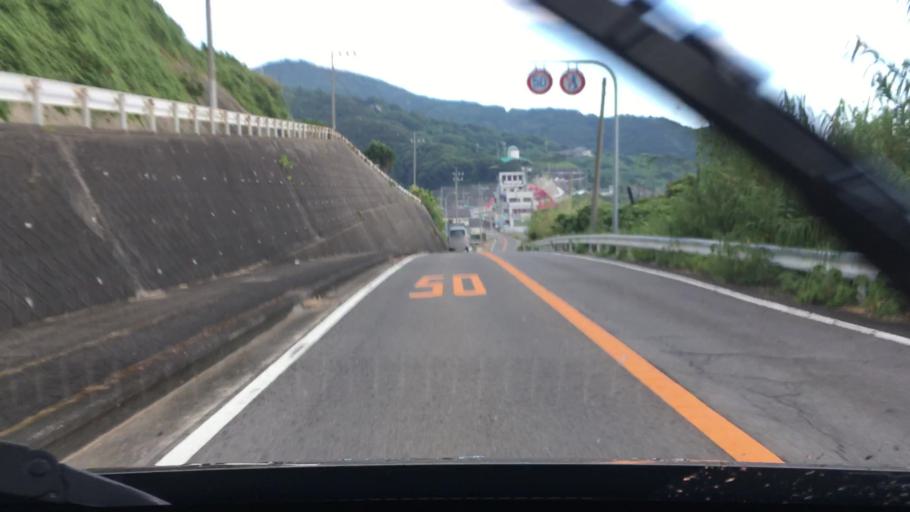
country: JP
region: Nagasaki
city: Togitsu
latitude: 32.8835
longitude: 129.6786
